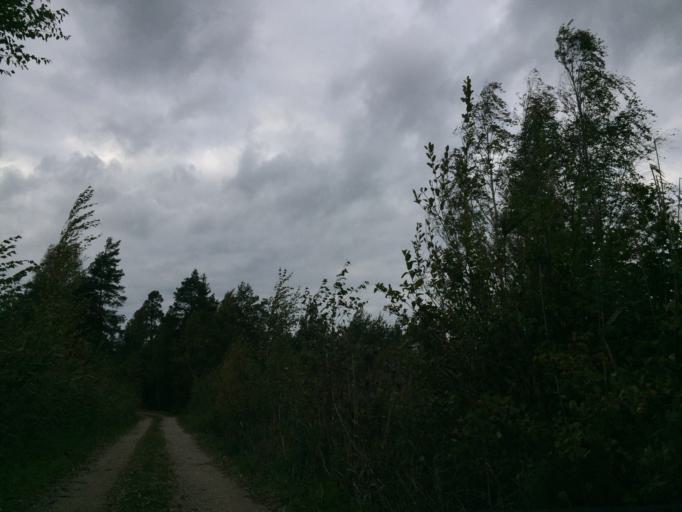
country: LV
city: Tireli
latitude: 56.8989
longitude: 23.5165
